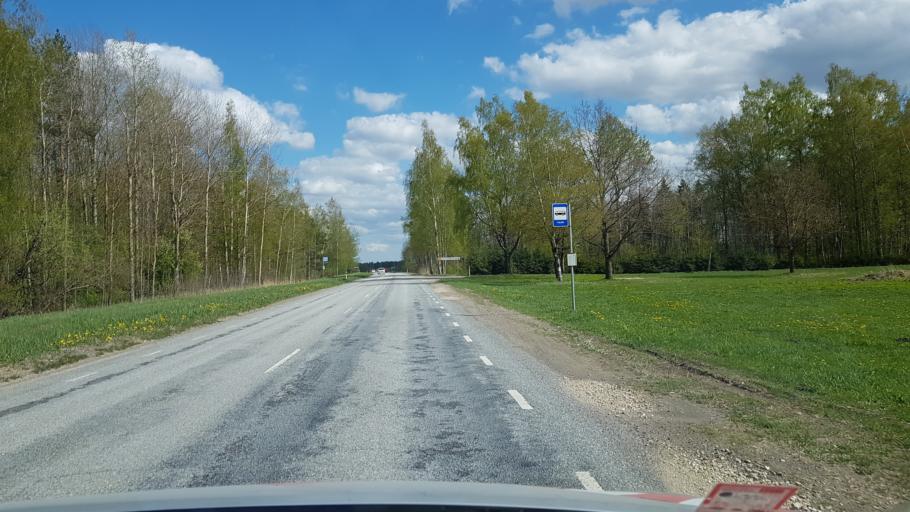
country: EE
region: Tartu
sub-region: UElenurme vald
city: Ulenurme
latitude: 58.3289
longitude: 26.7412
